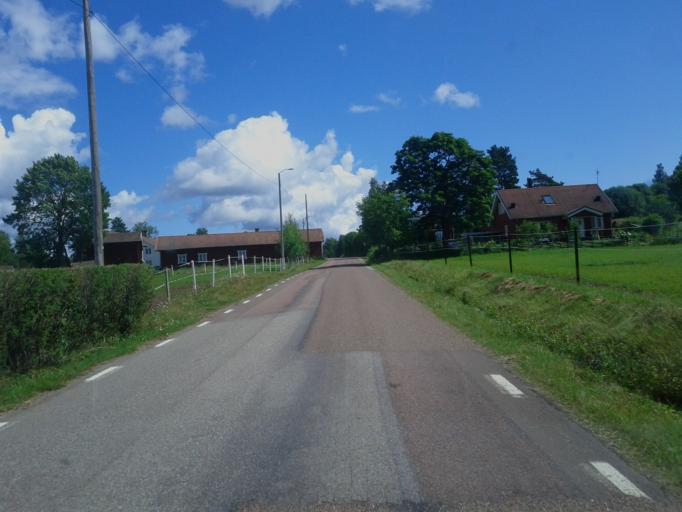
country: SE
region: Dalarna
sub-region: Rattviks Kommun
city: Vikarbyn
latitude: 60.9159
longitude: 15.0613
